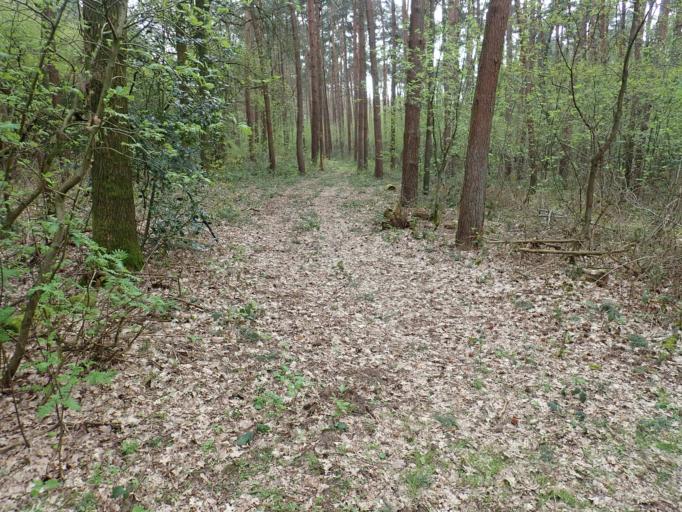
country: BE
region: Flanders
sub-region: Provincie Antwerpen
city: Kasterlee
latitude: 51.2266
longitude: 4.9361
